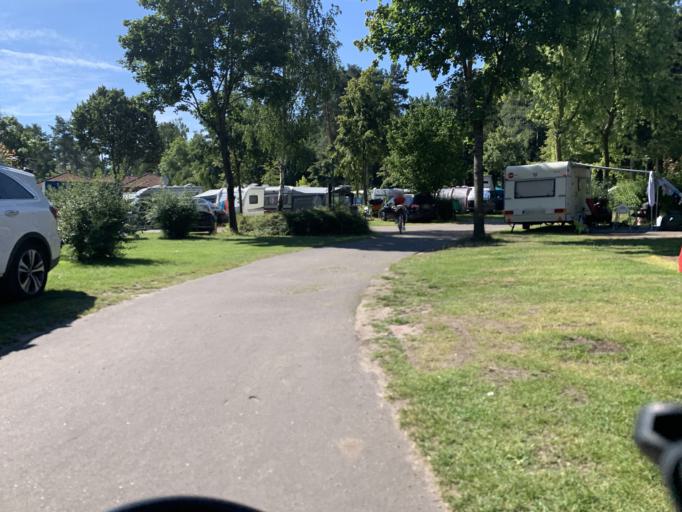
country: DE
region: Lower Saxony
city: Wietzendorf
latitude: 52.9355
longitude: 9.9600
